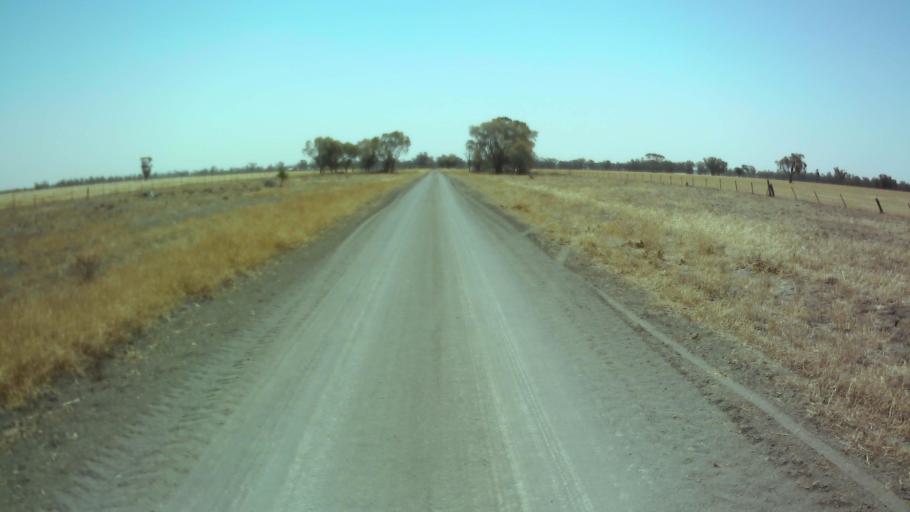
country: AU
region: New South Wales
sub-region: Weddin
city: Grenfell
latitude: -33.9910
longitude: 147.8636
